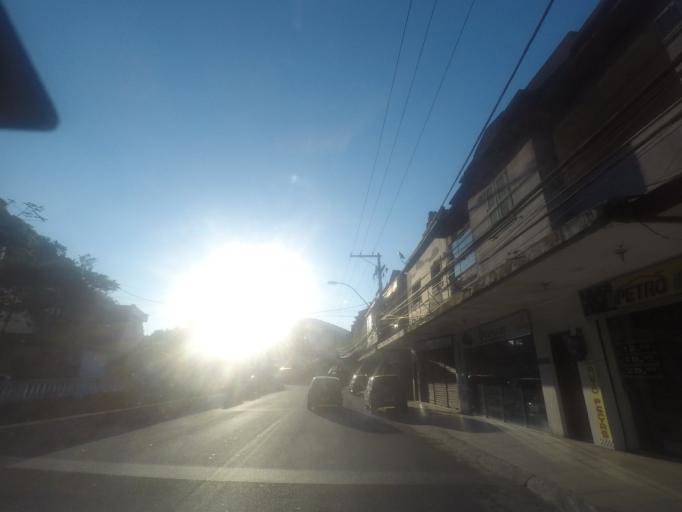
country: BR
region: Rio de Janeiro
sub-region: Petropolis
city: Petropolis
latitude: -22.5335
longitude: -43.2006
